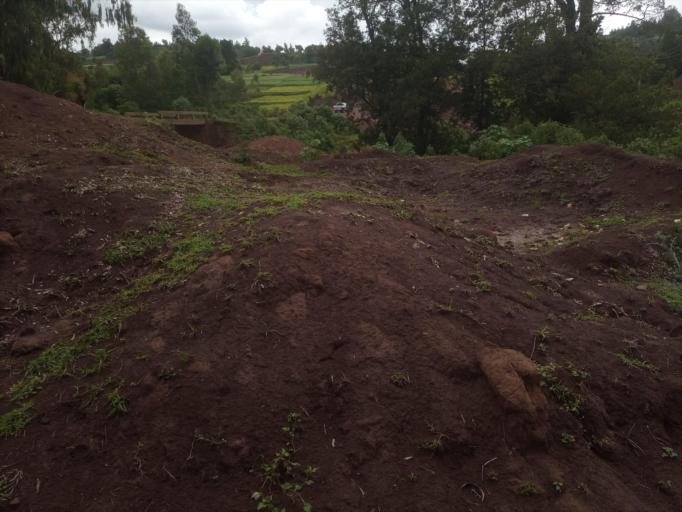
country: ET
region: Southern Nations, Nationalities, and People's Region
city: K'olito
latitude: 7.3761
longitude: 37.8850
